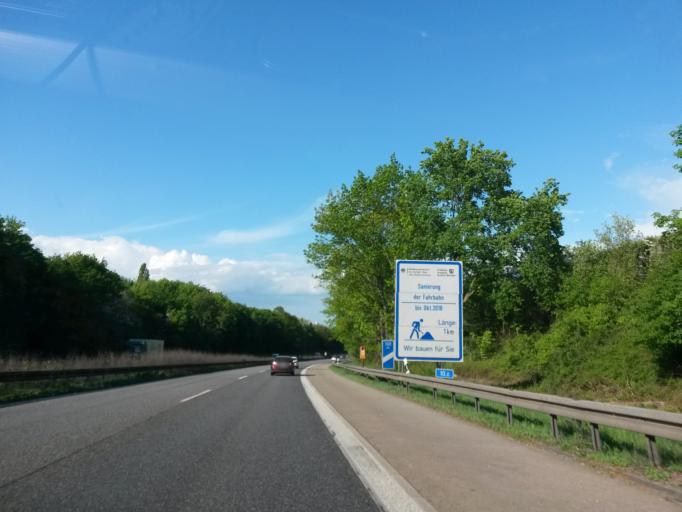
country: DE
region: North Rhine-Westphalia
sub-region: Regierungsbezirk Koln
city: Bonn
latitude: 50.7116
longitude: 7.0620
